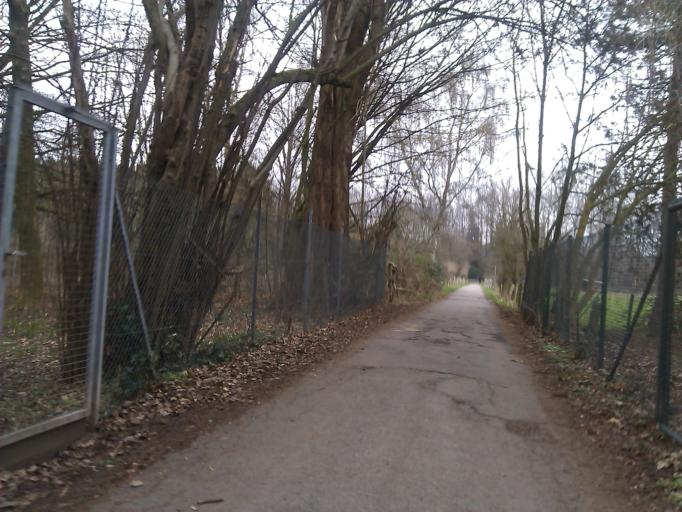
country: DE
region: North Rhine-Westphalia
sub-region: Regierungsbezirk Koln
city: Porz am Rhein
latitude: 50.8761
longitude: 7.0410
